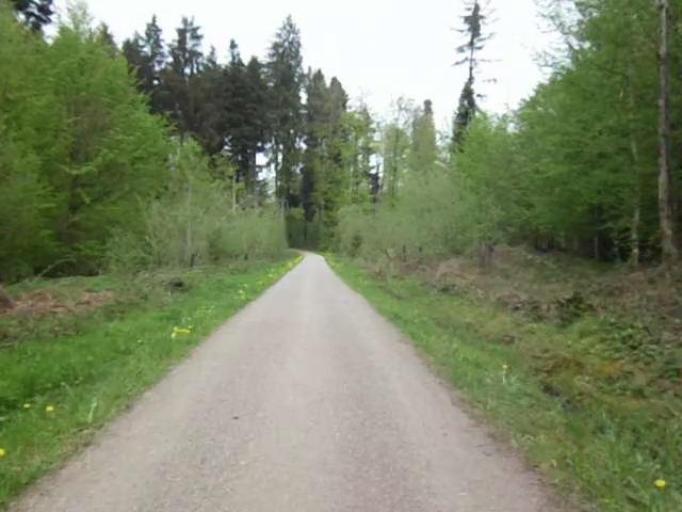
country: CH
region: Zurich
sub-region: Bezirk Hinwil
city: Rueti / Westlicher Dorfteil
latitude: 47.2547
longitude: 8.8360
